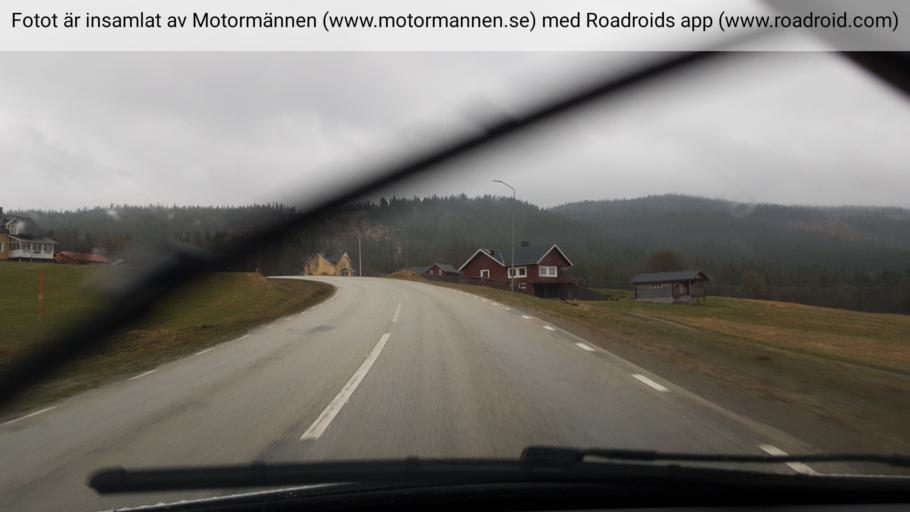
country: SE
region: Jaemtland
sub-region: Bergs Kommun
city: Hoverberg
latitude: 62.5302
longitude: 14.2021
